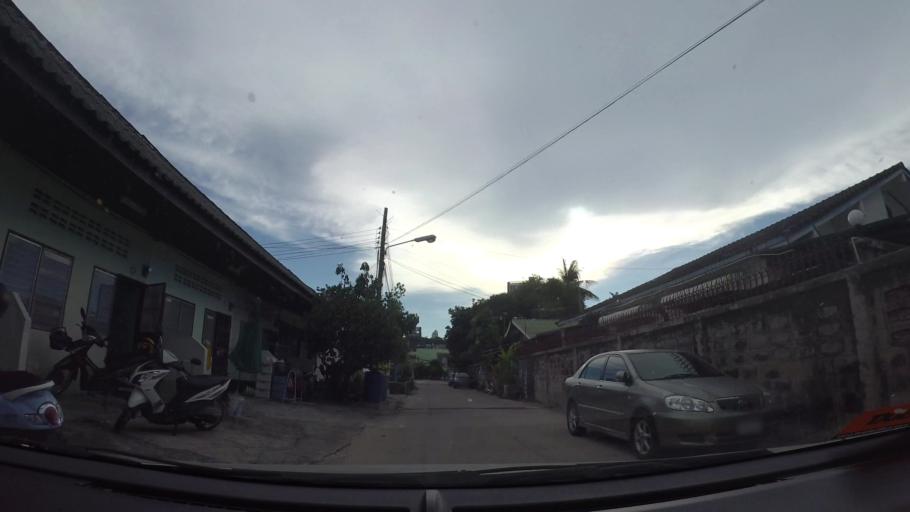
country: TH
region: Chon Buri
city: Phatthaya
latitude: 12.9177
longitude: 100.8763
